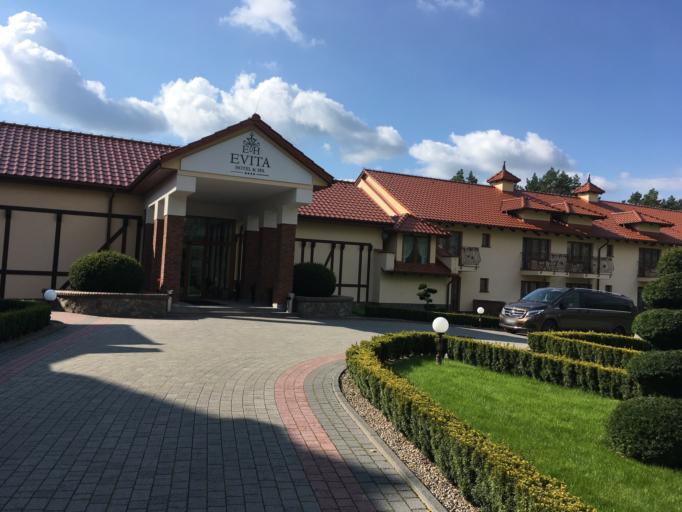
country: PL
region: Kujawsko-Pomorskie
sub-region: Powiat swiecki
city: Osie
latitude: 53.6200
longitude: 18.2594
